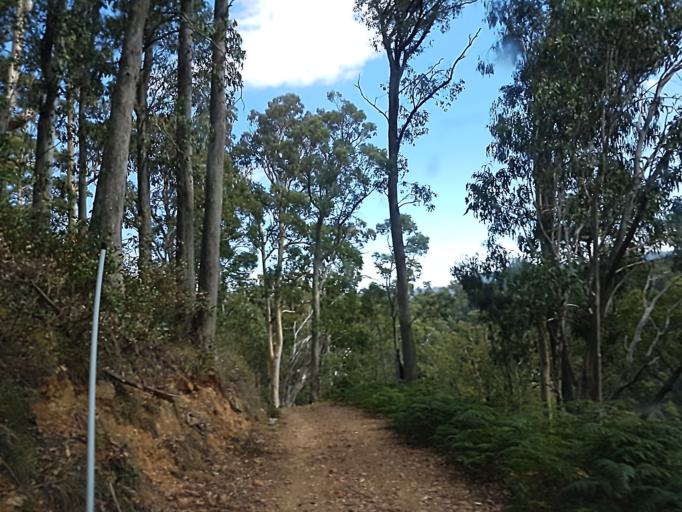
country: AU
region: Victoria
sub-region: Alpine
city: Mount Beauty
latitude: -36.9149
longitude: 146.9997
